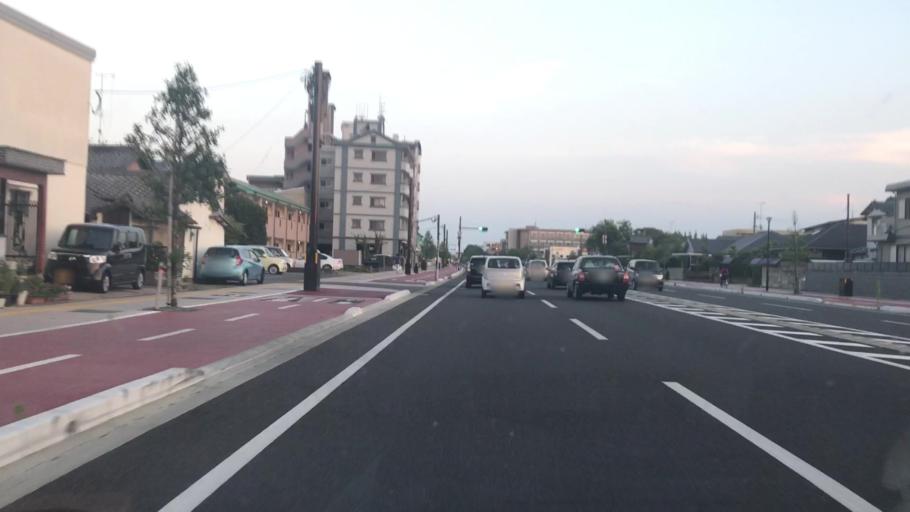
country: JP
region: Saga Prefecture
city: Saga-shi
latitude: 33.2477
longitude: 130.2930
